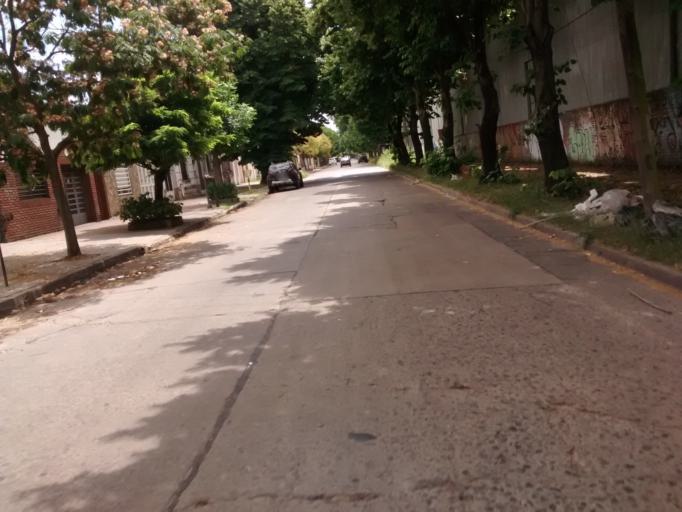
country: AR
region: Buenos Aires
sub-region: Partido de La Plata
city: La Plata
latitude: -34.9439
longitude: -57.9441
